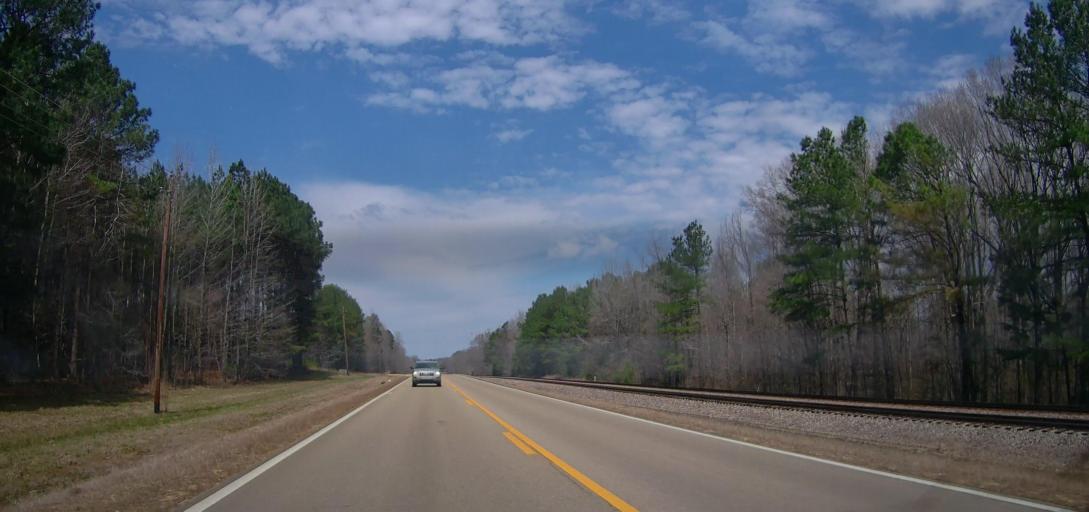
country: US
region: Mississippi
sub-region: Union County
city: New Albany
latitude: 34.5860
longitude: -89.1332
